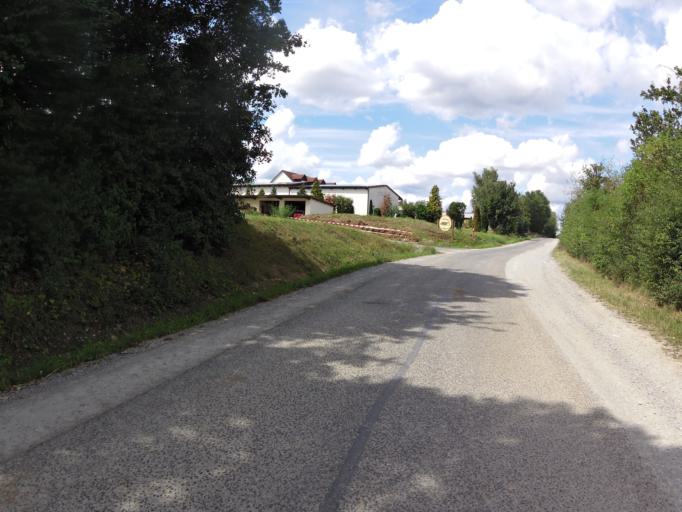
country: DE
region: Bavaria
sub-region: Regierungsbezirk Unterfranken
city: Sommerhausen
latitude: 49.6999
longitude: 10.0379
